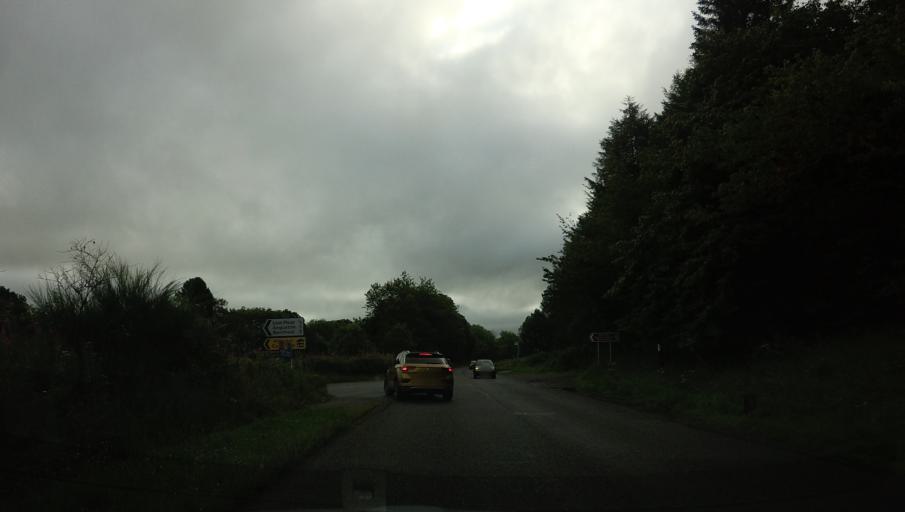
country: GB
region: Scotland
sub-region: Aberdeenshire
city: Westhill
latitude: 57.1021
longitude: -2.2925
